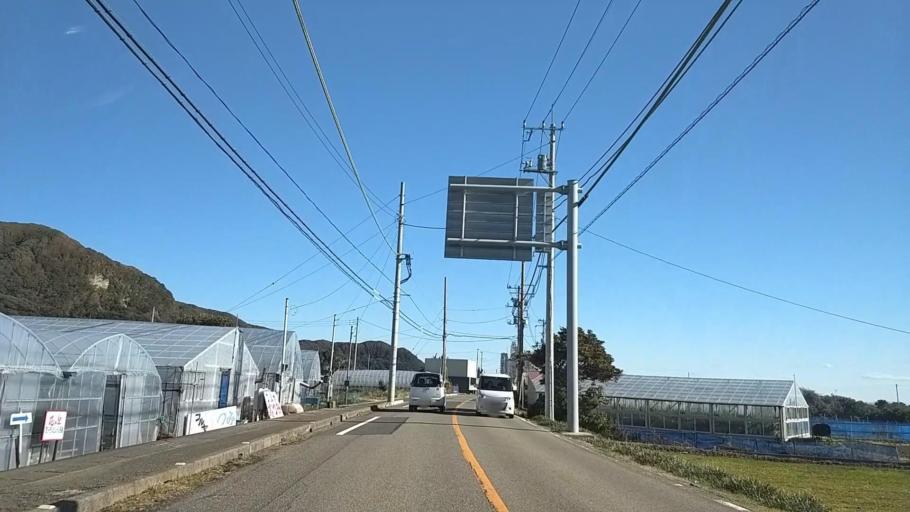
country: JP
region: Chiba
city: Tateyama
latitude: 34.9094
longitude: 139.9116
